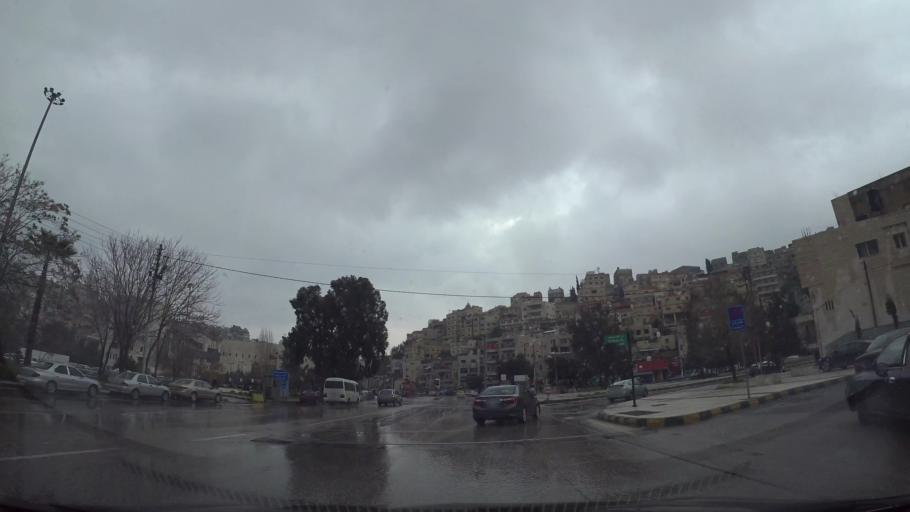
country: JO
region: Amman
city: Amman
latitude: 31.9445
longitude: 35.9221
